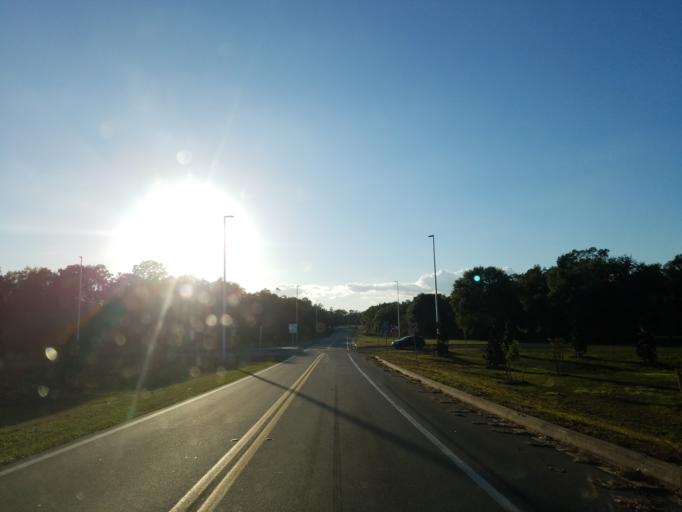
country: US
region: Florida
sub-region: Hernando County
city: Ridge Manor
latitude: 28.6020
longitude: -82.2050
